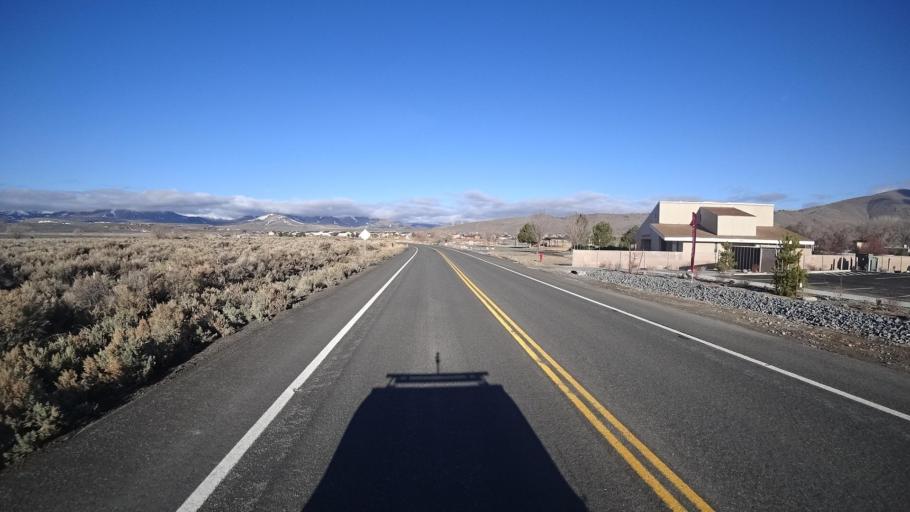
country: US
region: Nevada
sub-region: Washoe County
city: Cold Springs
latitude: 39.6754
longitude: -119.9756
